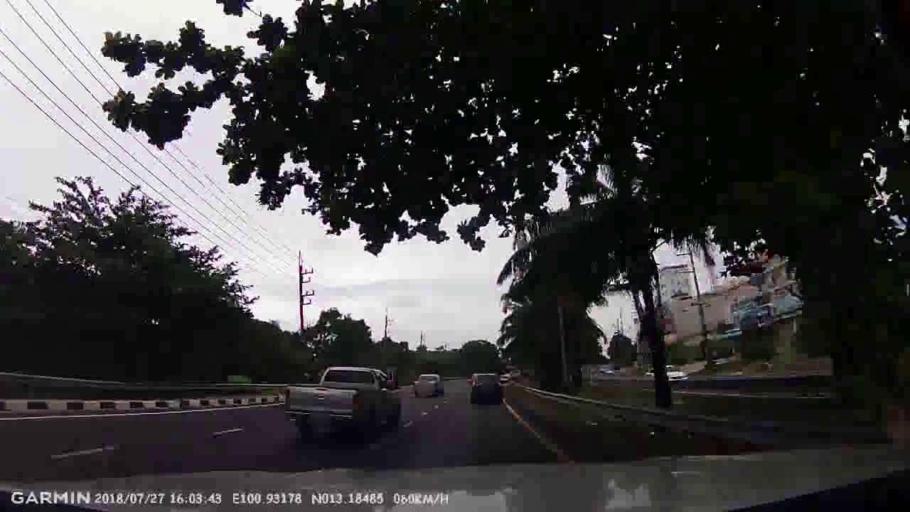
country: TH
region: Chon Buri
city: Si Racha
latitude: 13.1849
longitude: 100.9318
